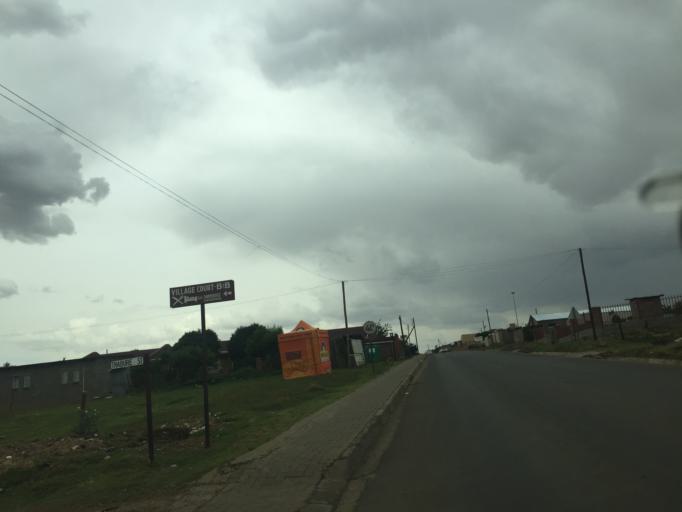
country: LS
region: Maseru
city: Maseru
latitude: -29.2780
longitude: 27.5299
